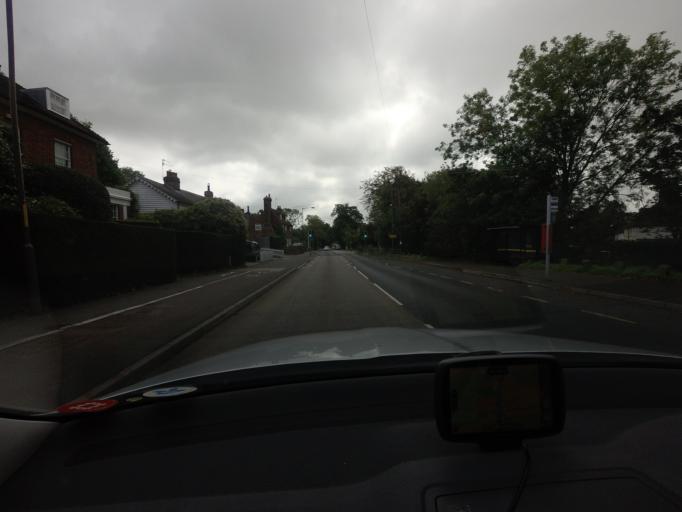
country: GB
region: England
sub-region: Kent
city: Tonbridge
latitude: 51.2135
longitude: 0.2487
